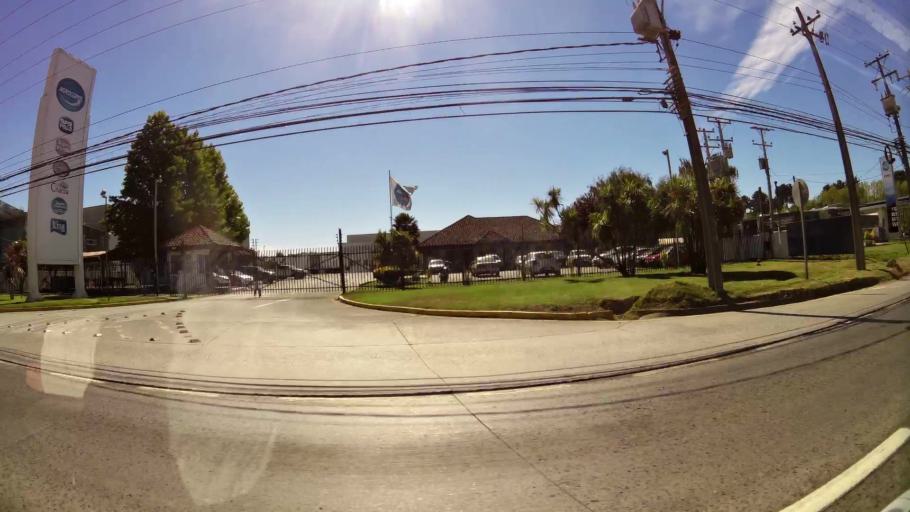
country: CL
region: Biobio
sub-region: Provincia de Concepcion
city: Penco
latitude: -36.7768
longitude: -73.0178
